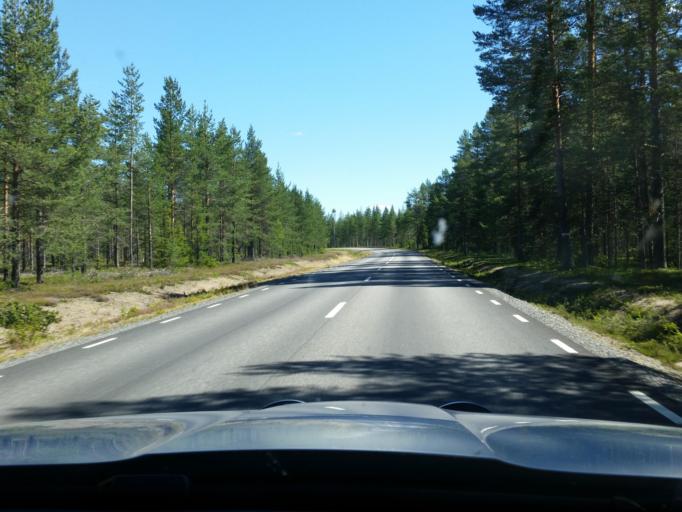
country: SE
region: Vaesterbotten
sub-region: Skelleftea Kommun
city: Storvik
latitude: 65.3356
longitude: 20.8819
